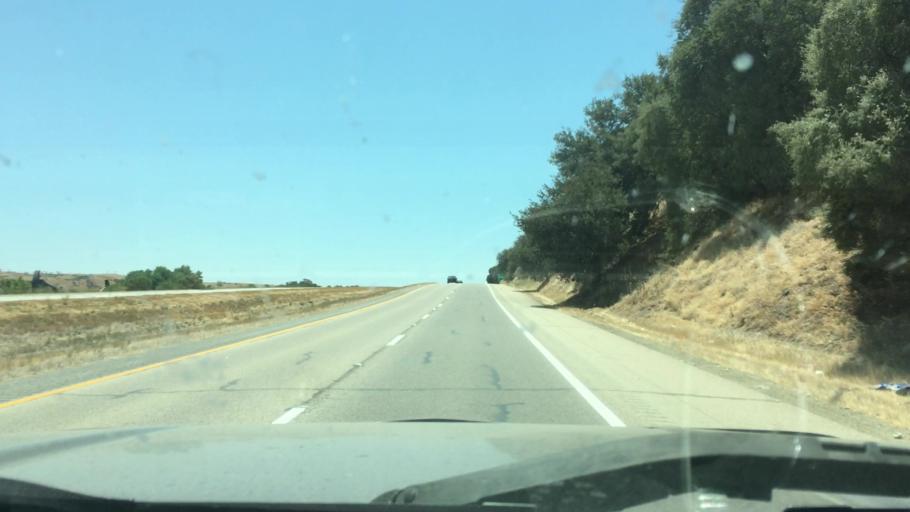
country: US
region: California
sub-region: San Luis Obispo County
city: Lake Nacimiento
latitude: 35.9541
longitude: -120.8806
